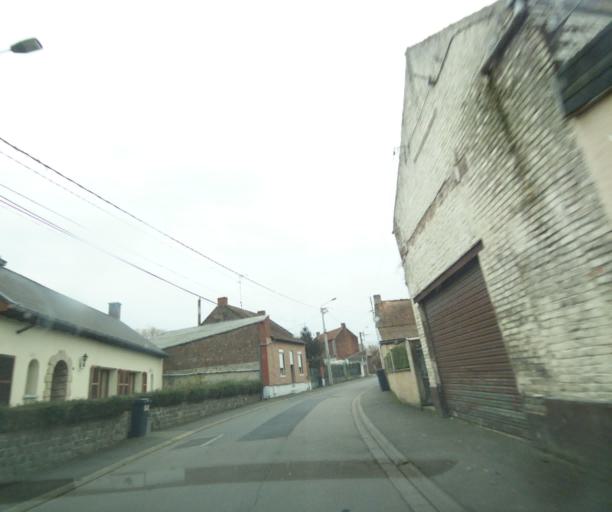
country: FR
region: Nord-Pas-de-Calais
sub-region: Departement du Nord
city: Crespin
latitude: 50.4208
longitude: 3.6566
